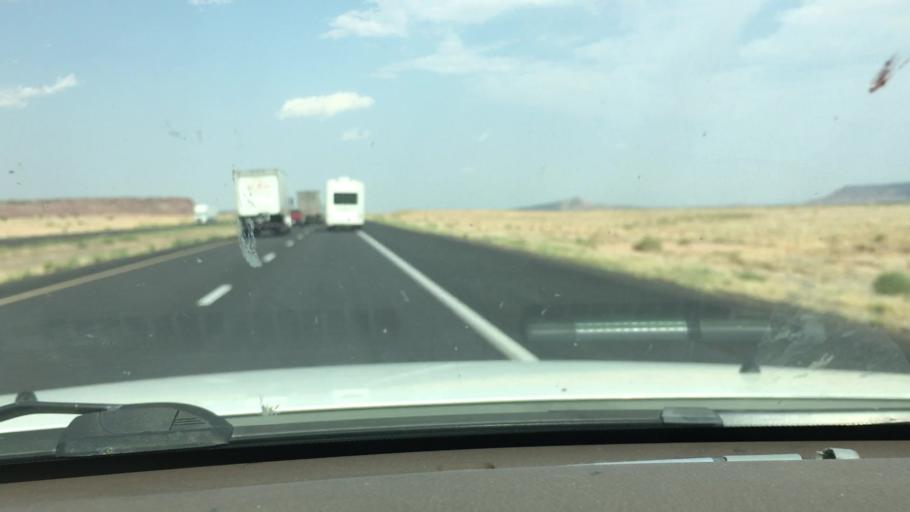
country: US
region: New Mexico
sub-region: Cibola County
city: Laguna
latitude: 34.9918
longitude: -107.2298
